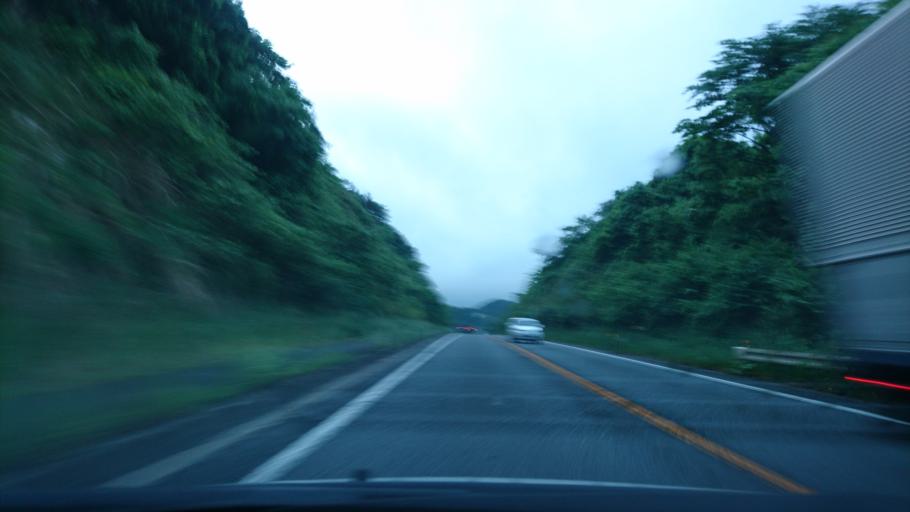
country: JP
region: Iwate
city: Ichinoseki
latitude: 38.8953
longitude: 141.1154
